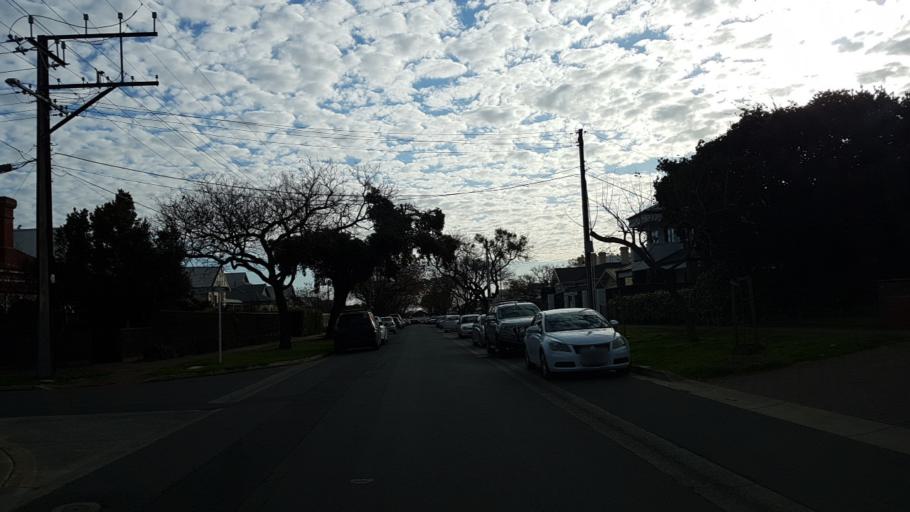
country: AU
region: South Australia
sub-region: Prospect
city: Prospect
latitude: -34.8869
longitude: 138.5978
